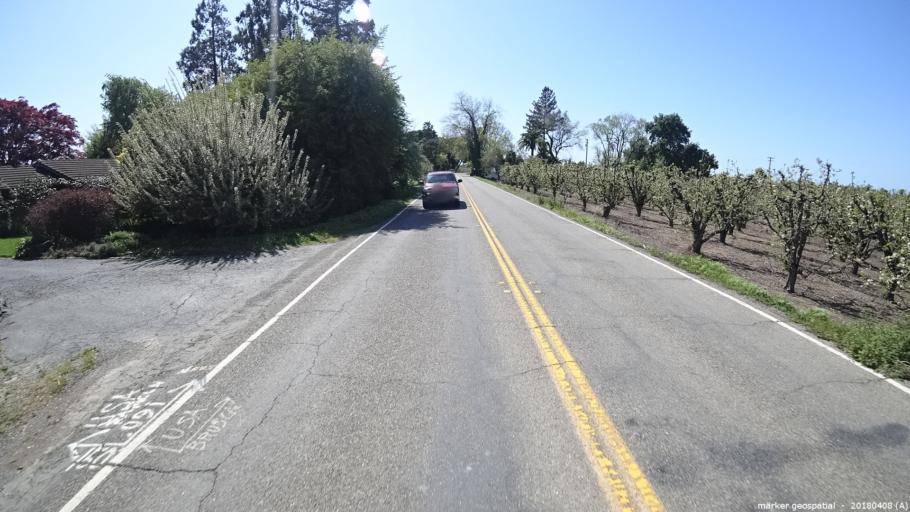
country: US
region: California
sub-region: Sacramento County
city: Walnut Grove
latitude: 38.3357
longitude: -121.5525
